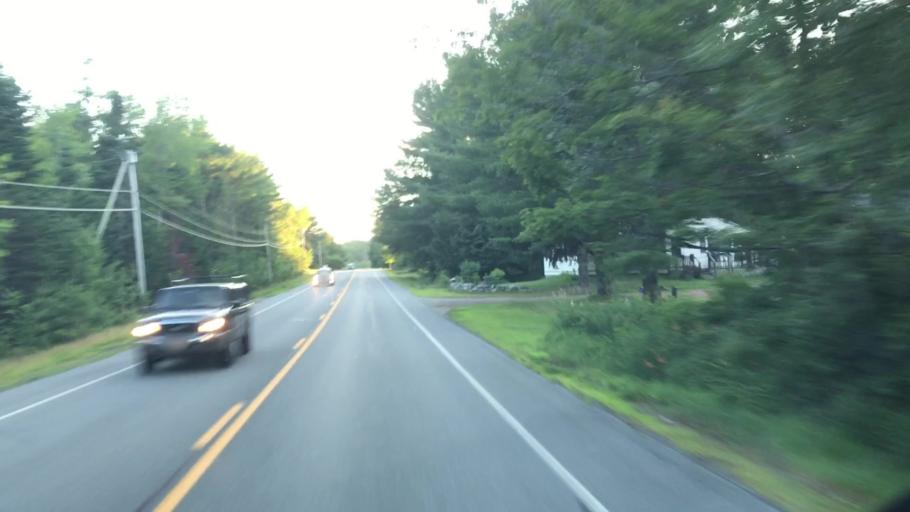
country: US
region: Maine
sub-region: Penobscot County
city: Lincoln
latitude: 45.3780
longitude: -68.4562
